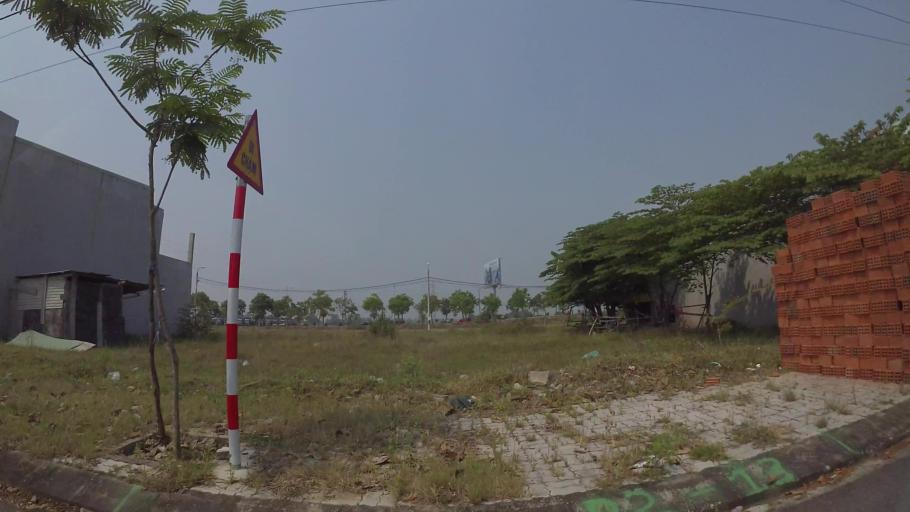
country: VN
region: Da Nang
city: Cam Le
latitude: 15.9708
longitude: 108.2104
